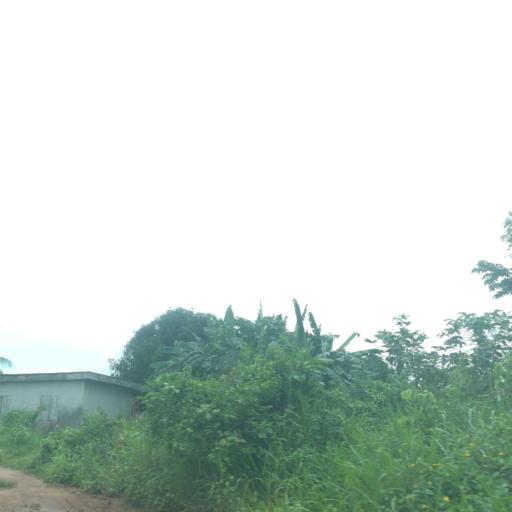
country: NG
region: Lagos
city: Ejirin
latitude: 6.6592
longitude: 3.7258
